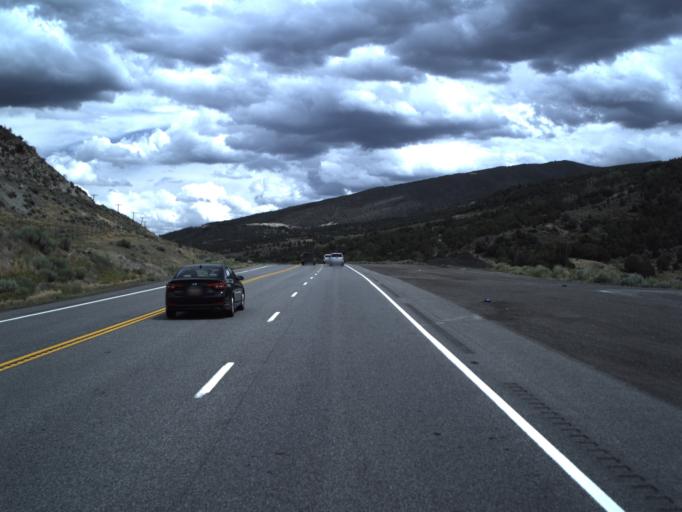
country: US
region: Utah
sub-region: Sanpete County
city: Fairview
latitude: 39.9291
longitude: -111.1894
